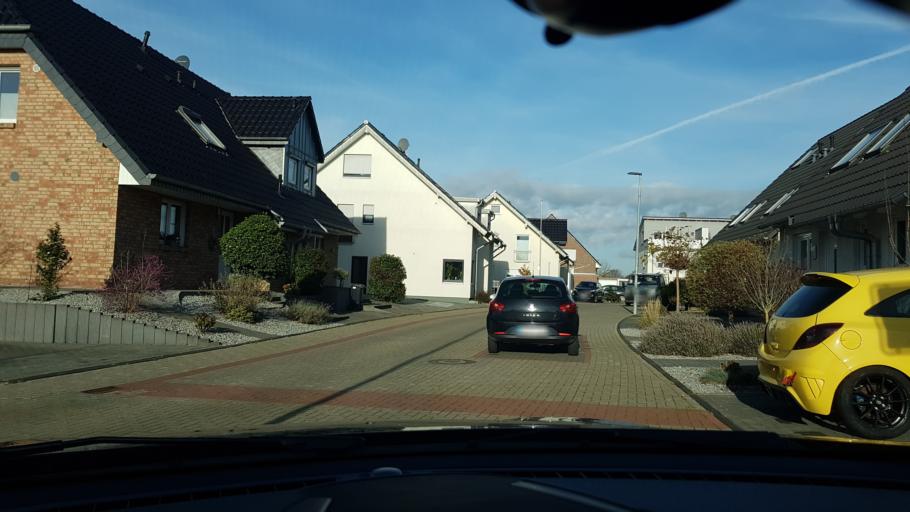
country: DE
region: North Rhine-Westphalia
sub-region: Regierungsbezirk Dusseldorf
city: Grevenbroich
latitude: 51.1172
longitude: 6.5577
